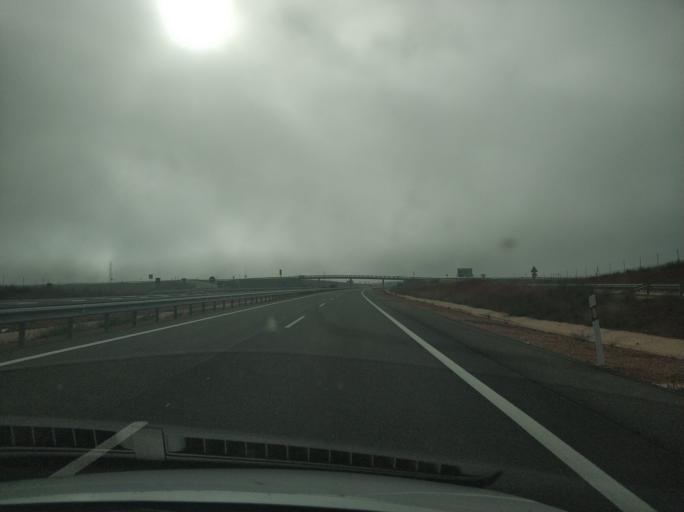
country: ES
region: Castille and Leon
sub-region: Provincia de Soria
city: Alcubilla de las Penas
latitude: 41.2637
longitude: -2.4739
